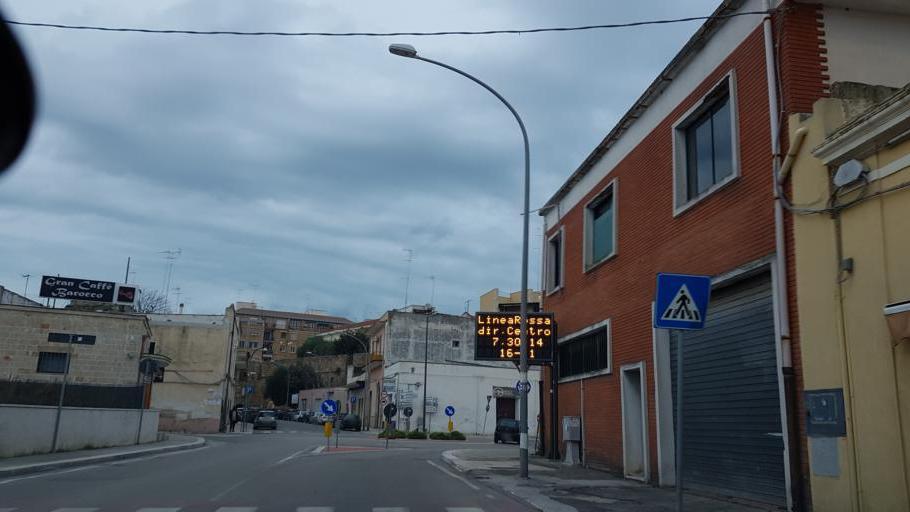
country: IT
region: Apulia
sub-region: Provincia di Brindisi
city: Brindisi
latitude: 40.6317
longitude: 17.9461
